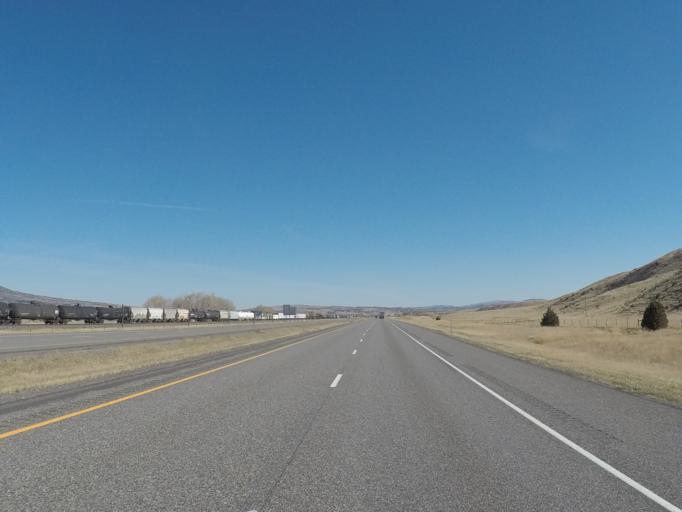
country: US
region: Montana
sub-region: Park County
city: Livingston
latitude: 45.7127
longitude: -110.4349
